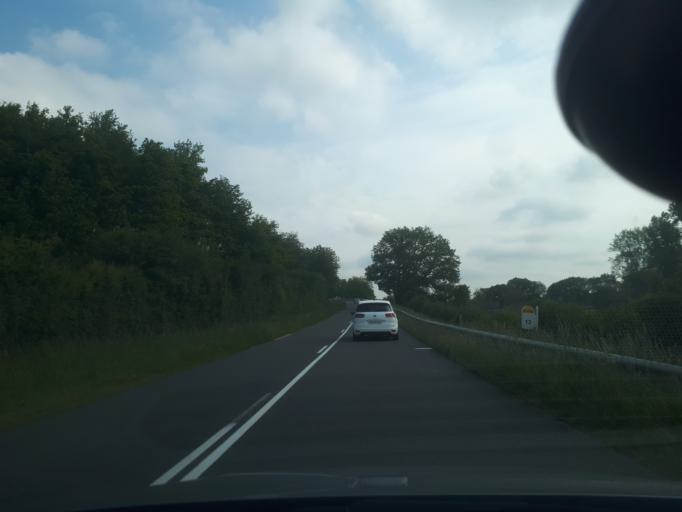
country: FR
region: Auvergne
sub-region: Departement de l'Allier
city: Dompierre-sur-Besbre
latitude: 46.4253
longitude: 3.6181
